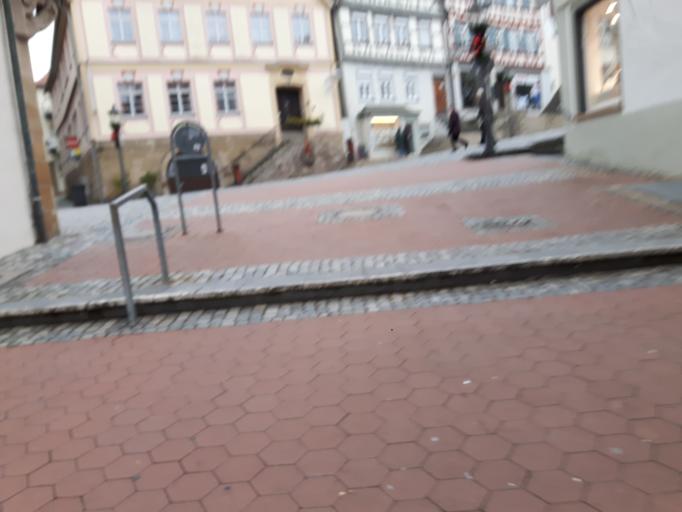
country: DE
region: Baden-Wuerttemberg
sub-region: Regierungsbezirk Stuttgart
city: Backnang
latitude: 48.9466
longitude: 9.4305
